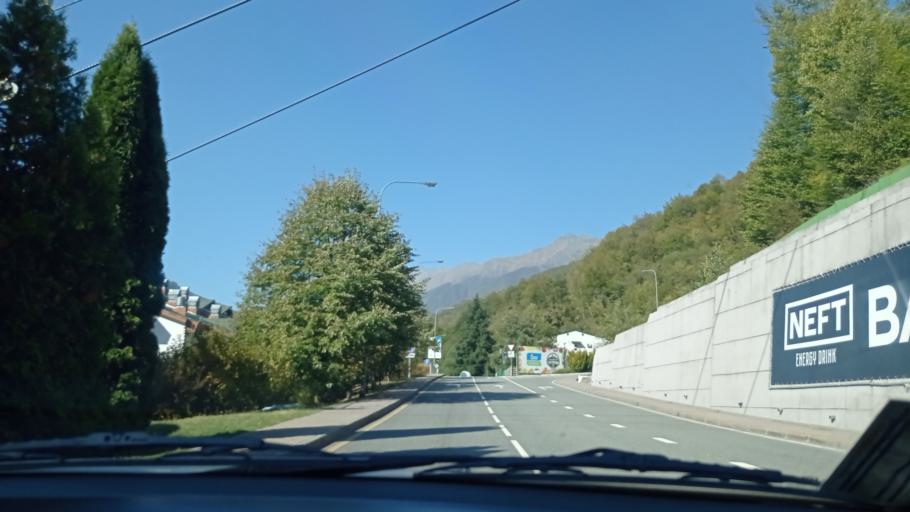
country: RU
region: Krasnodarskiy
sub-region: Sochi City
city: Krasnaya Polyana
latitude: 43.6851
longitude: 40.2809
